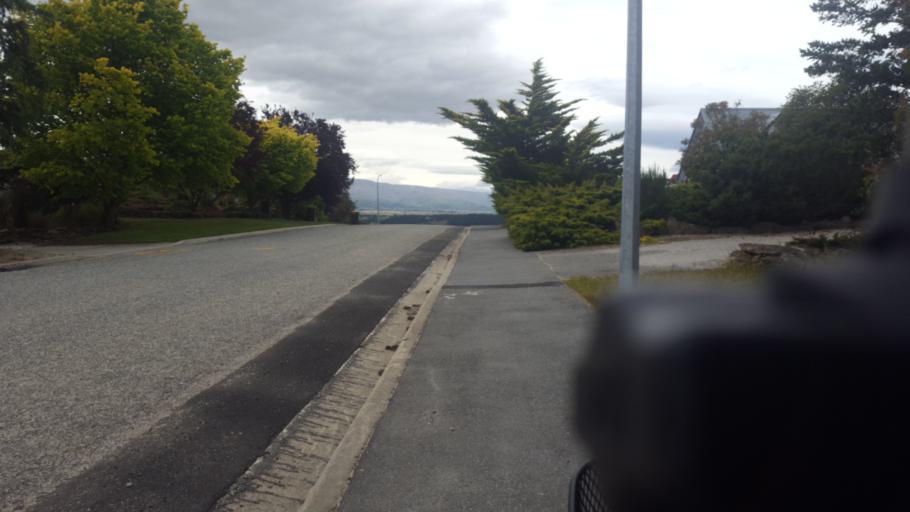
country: NZ
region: Otago
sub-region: Queenstown-Lakes District
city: Wanaka
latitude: -45.2615
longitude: 169.3775
